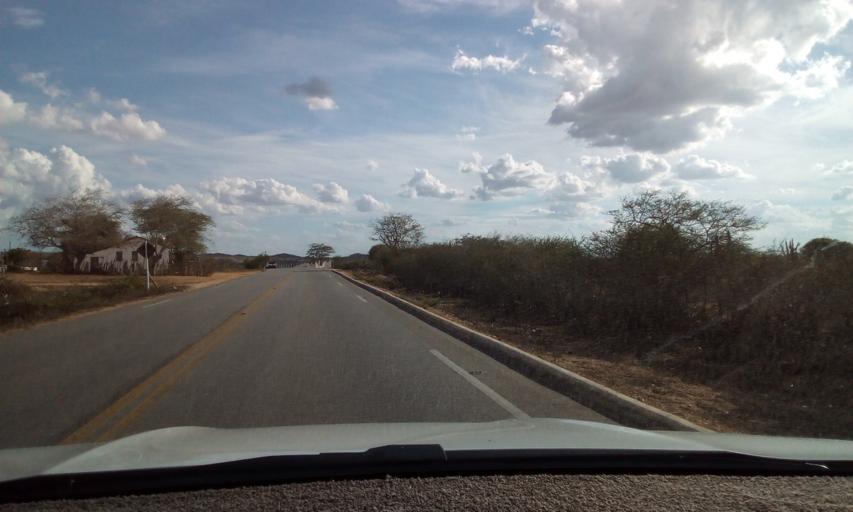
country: BR
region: Paraiba
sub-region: Soledade
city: Soledade
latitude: -6.9435
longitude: -36.3856
